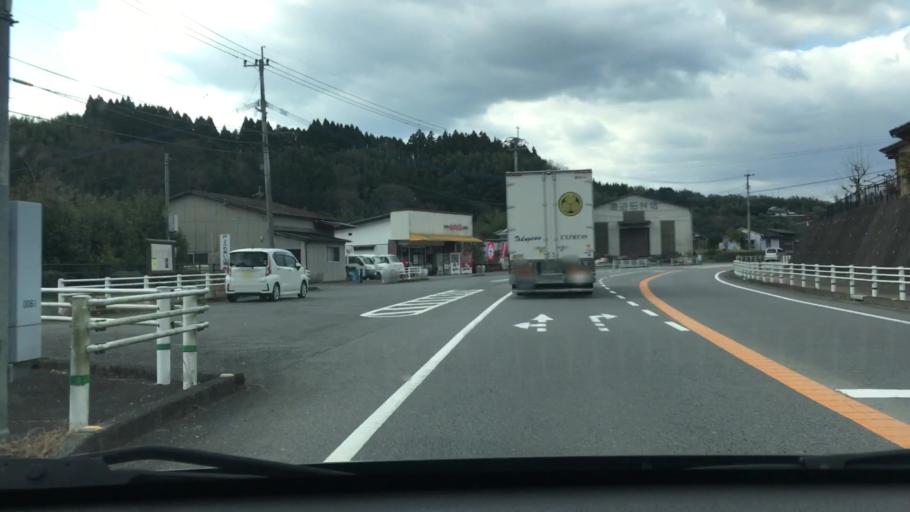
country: JP
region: Oita
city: Usuki
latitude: 33.0651
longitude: 131.6599
